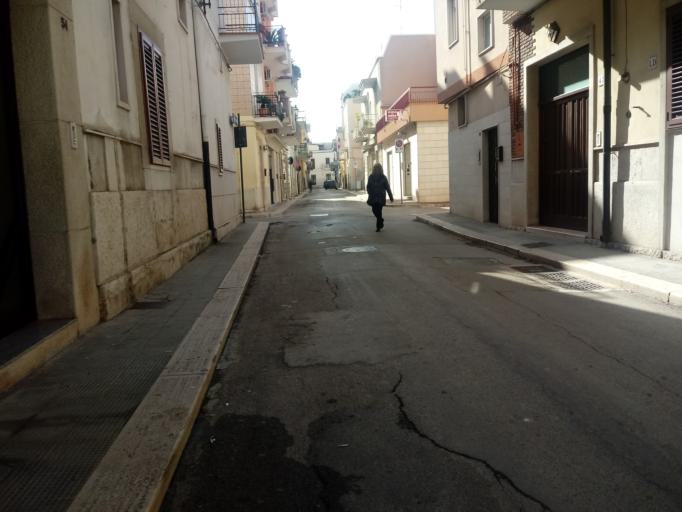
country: IT
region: Apulia
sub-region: Provincia di Barletta - Andria - Trani
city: Andria
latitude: 41.2226
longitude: 16.2966
